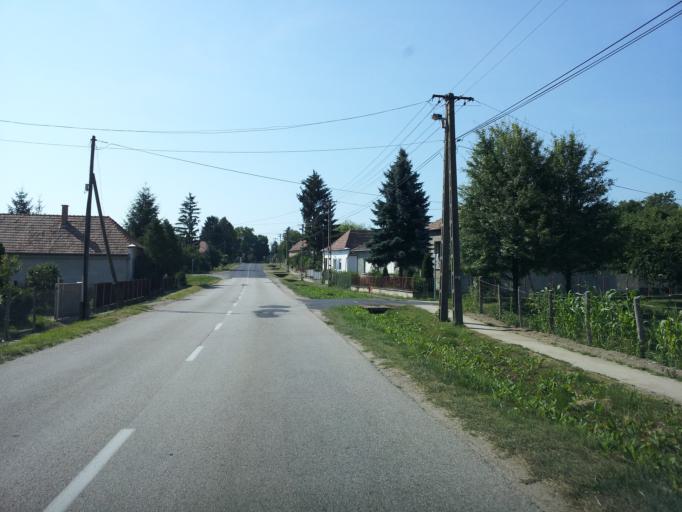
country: HU
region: Fejer
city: Lovasbereny
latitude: 47.3673
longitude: 18.5780
